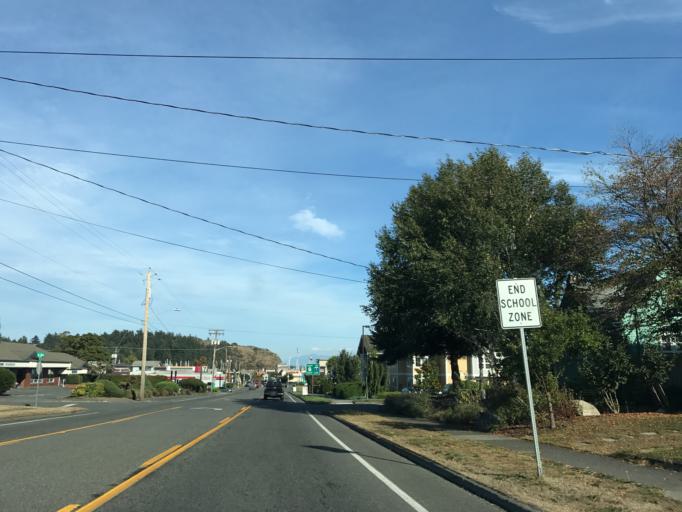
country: US
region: Washington
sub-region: Skagit County
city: Anacortes
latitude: 48.5126
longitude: -122.6166
